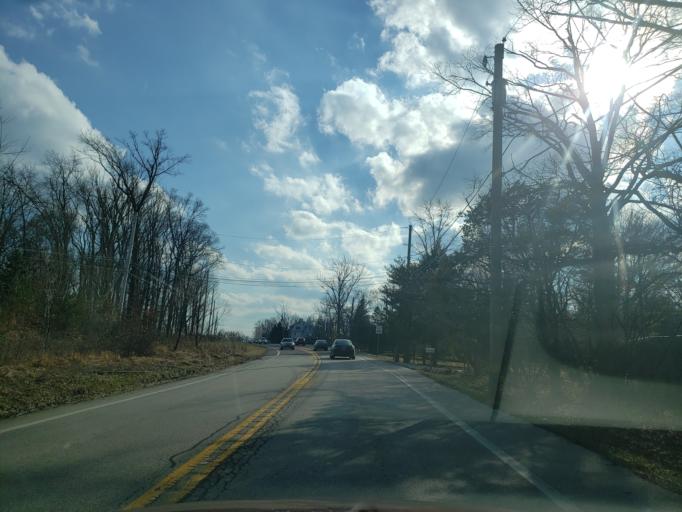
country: US
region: Pennsylvania
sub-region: Montgomery County
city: North Wales
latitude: 40.2074
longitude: -75.2549
